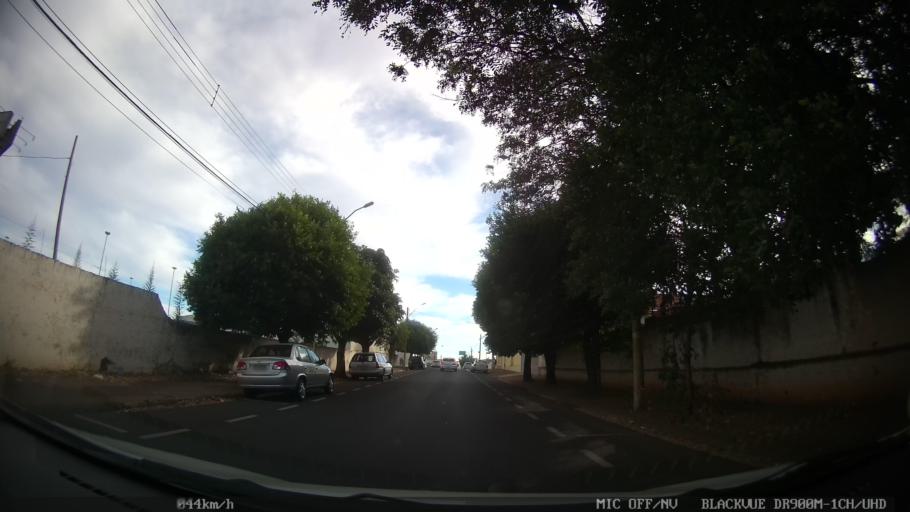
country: BR
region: Sao Paulo
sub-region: Catanduva
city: Catanduva
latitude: -21.1233
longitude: -48.9672
